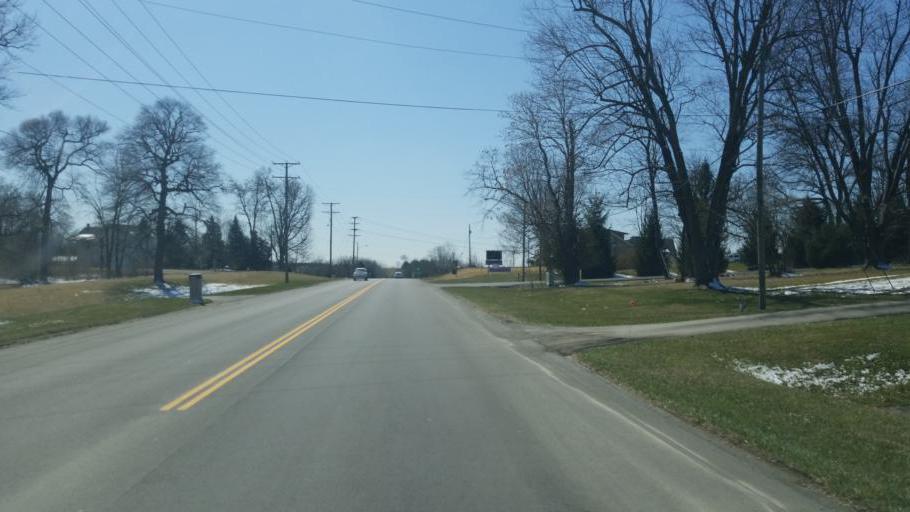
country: US
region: Ohio
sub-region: Highland County
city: Hillsboro
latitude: 39.1943
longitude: -83.6136
